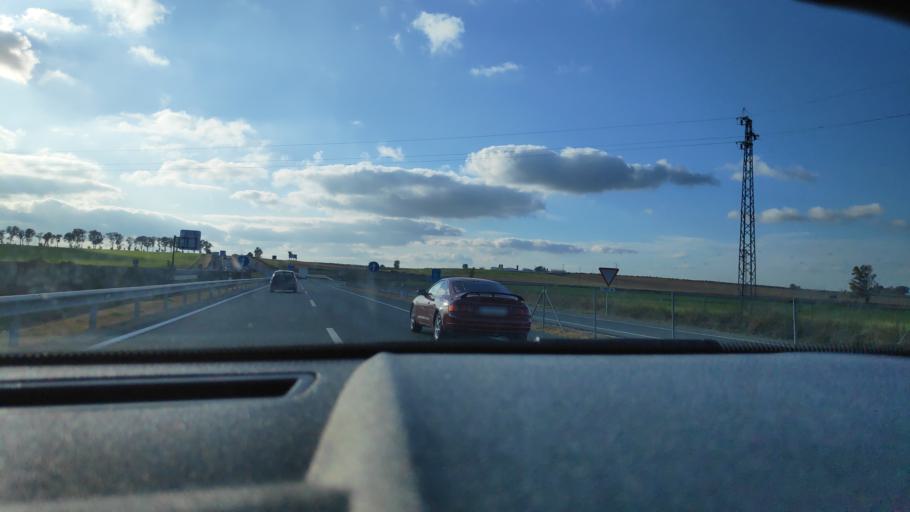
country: ES
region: Andalusia
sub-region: Provincia de Sevilla
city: La Campana
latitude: 37.5052
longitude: -5.4432
